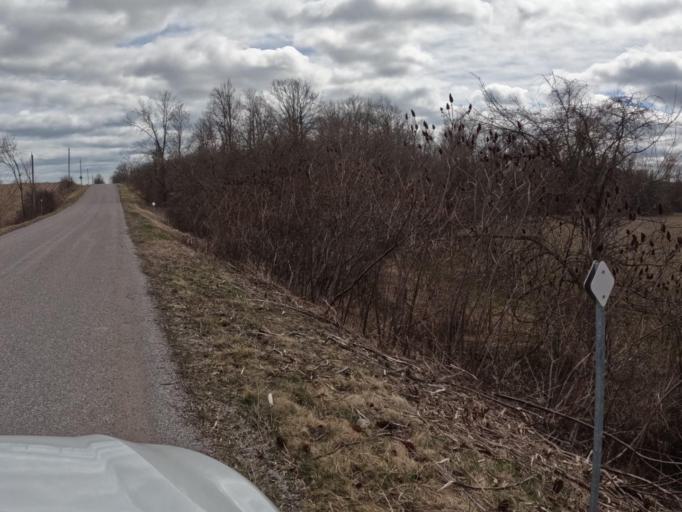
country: CA
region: Ontario
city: Norfolk County
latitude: 42.8533
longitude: -80.1712
